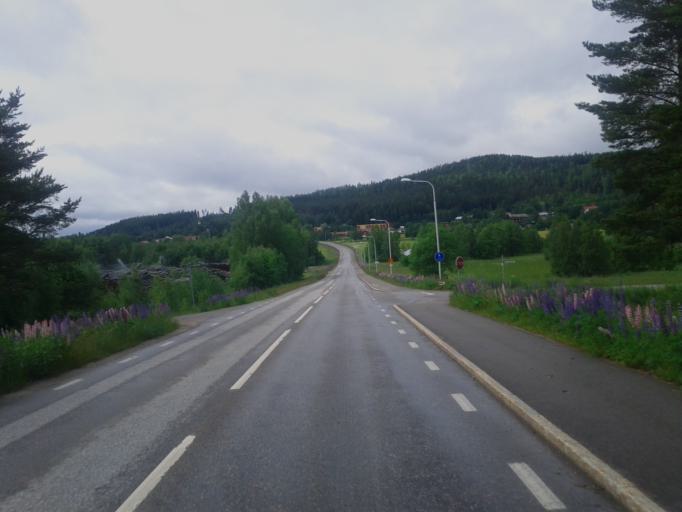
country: SE
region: Gaevleborg
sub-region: Hudiksvalls Kommun
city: Delsbo
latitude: 62.1028
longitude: 16.7221
